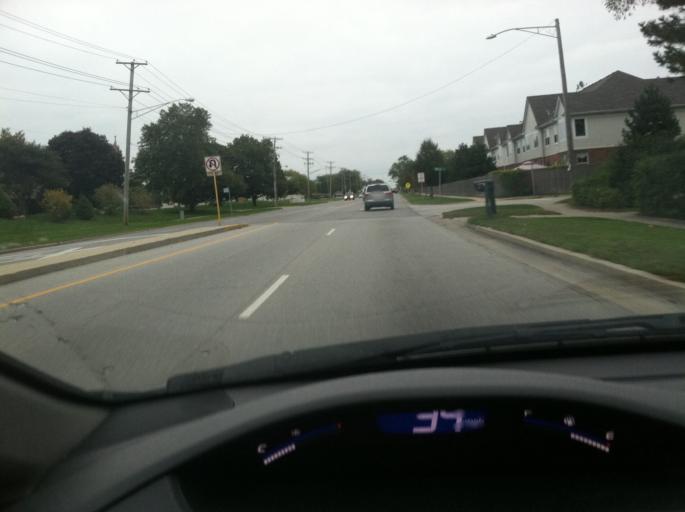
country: US
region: Illinois
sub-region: Cook County
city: Rosemont
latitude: 42.0096
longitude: -87.8837
